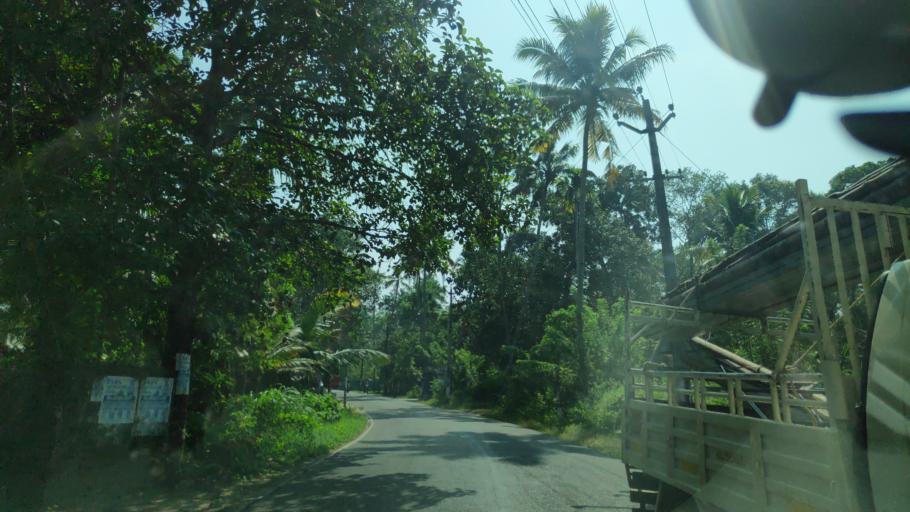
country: IN
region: Kerala
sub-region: Alappuzha
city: Vayalar
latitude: 9.6435
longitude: 76.2985
